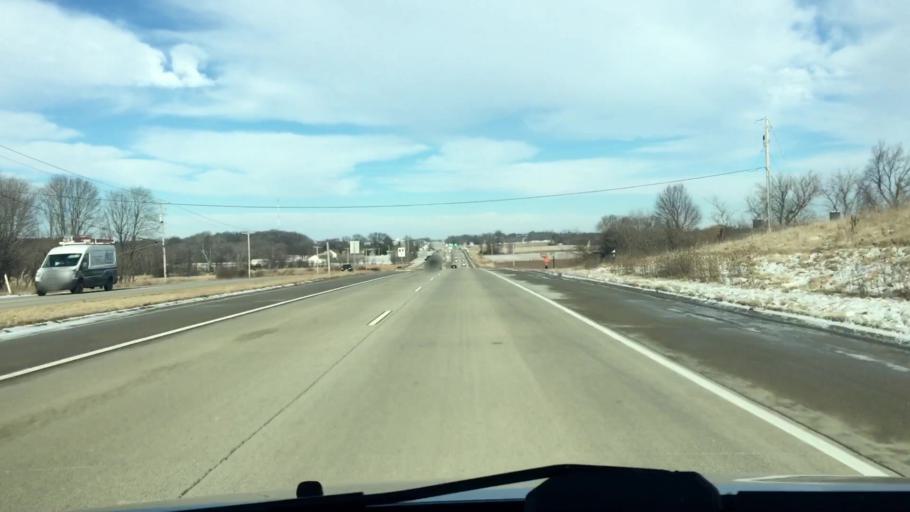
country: US
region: Wisconsin
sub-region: Waukesha County
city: Mukwonago
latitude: 42.9106
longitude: -88.3454
